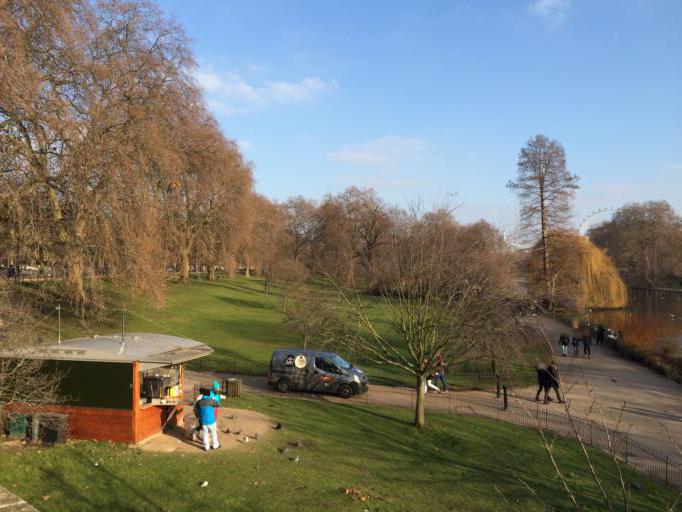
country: GB
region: England
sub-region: Greater London
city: London
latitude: 51.5017
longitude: -0.1393
